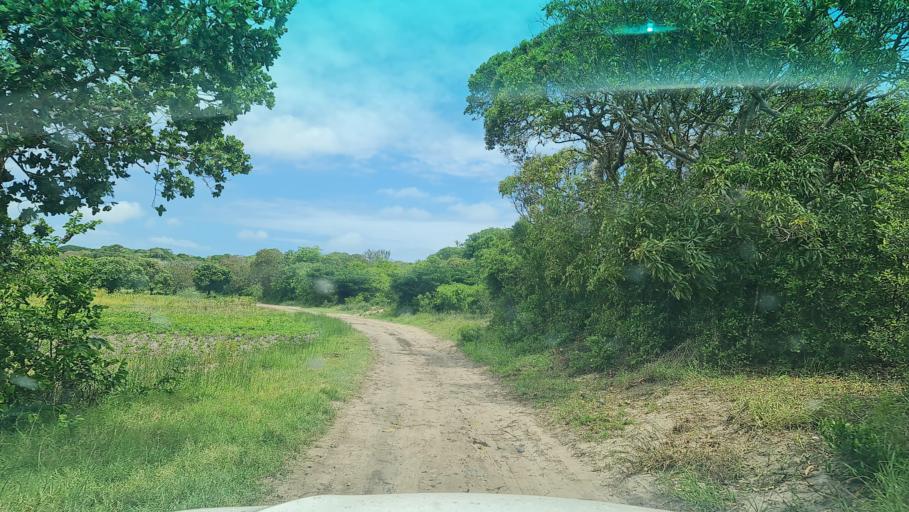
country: MZ
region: Maputo
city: Manhica
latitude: -25.5192
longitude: 32.8679
